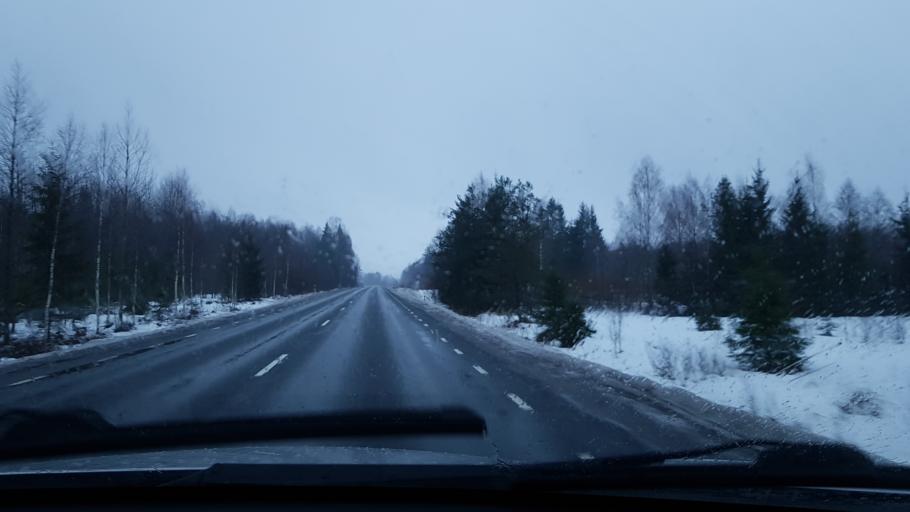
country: EE
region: Jaervamaa
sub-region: Tueri vald
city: Sarevere
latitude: 58.8033
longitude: 25.2232
